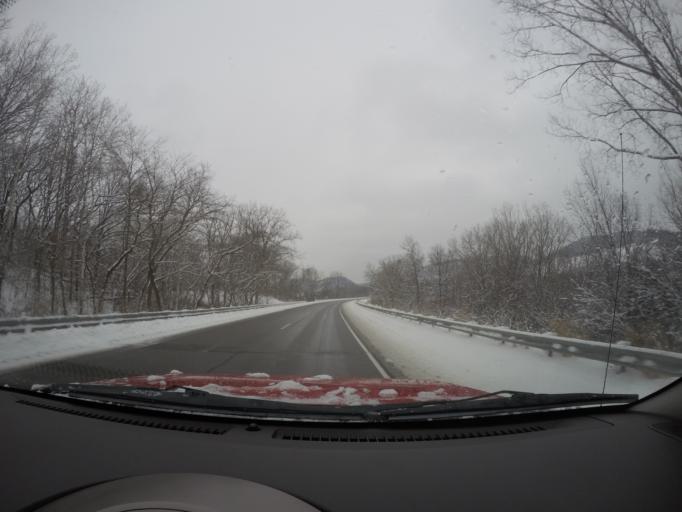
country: US
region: Wisconsin
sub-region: La Crosse County
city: Brice Prairie
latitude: 43.9166
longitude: -91.3667
